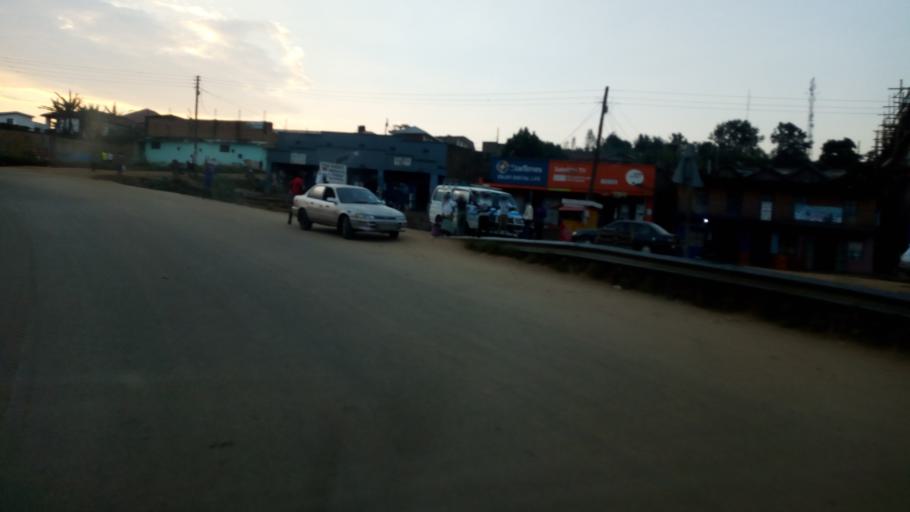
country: UG
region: Western Region
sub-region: Rukungiri District
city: Rukungiri
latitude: -0.7913
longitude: 29.9275
